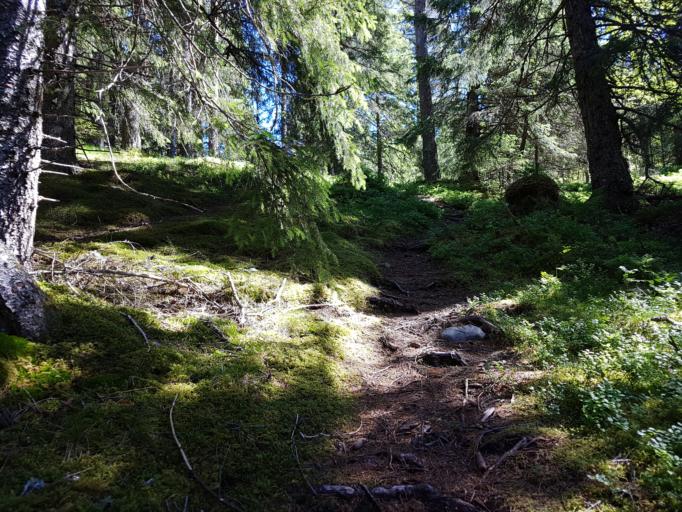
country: NO
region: Sor-Trondelag
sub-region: Skaun
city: Borsa
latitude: 63.4339
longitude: 10.1984
